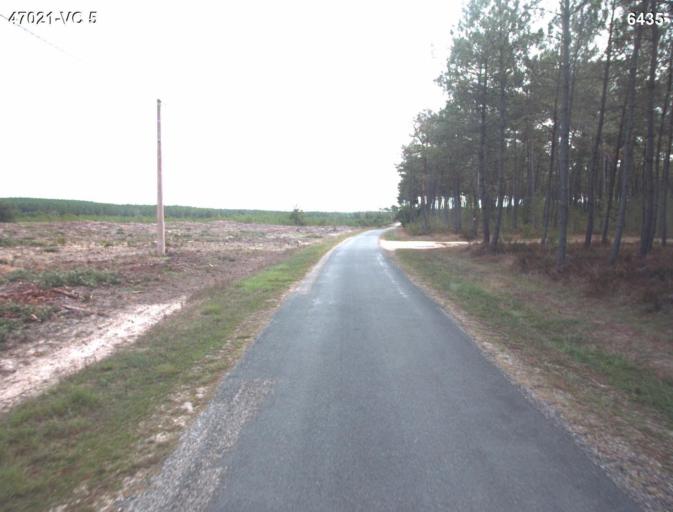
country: FR
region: Aquitaine
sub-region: Departement du Lot-et-Garonne
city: Barbaste
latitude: 44.1509
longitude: 0.2212
